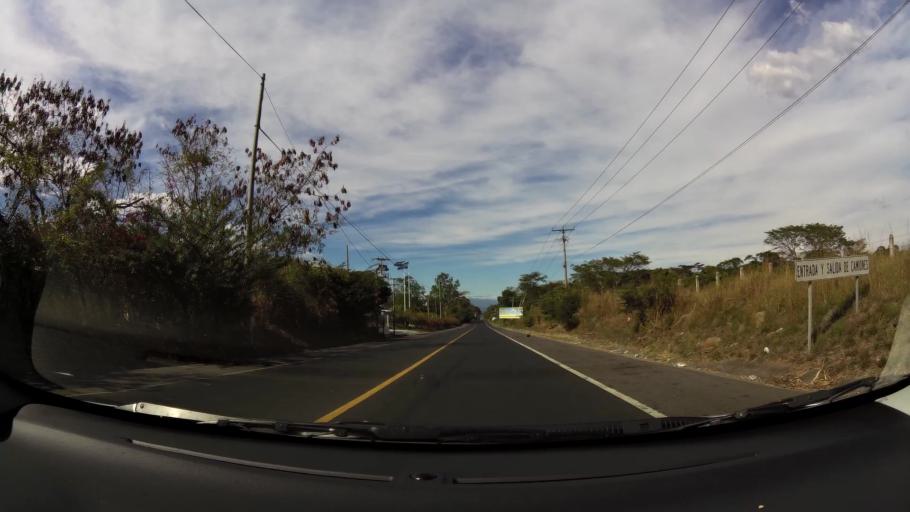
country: SV
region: San Salvador
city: Guazapa
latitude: 13.8946
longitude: -89.1777
